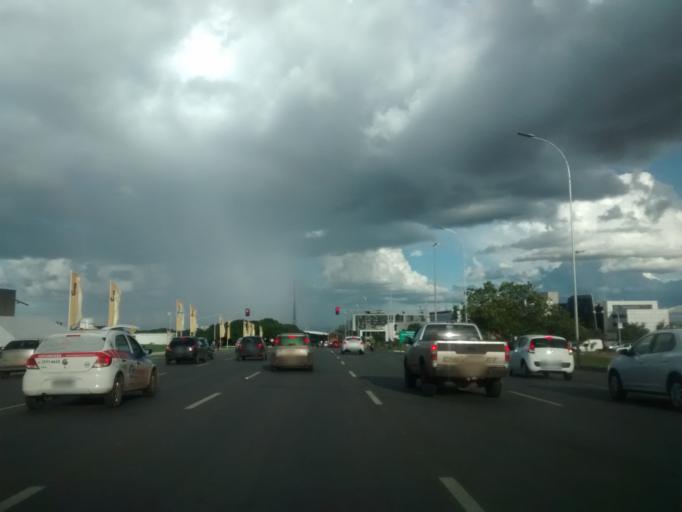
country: BR
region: Federal District
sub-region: Brasilia
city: Brasilia
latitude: -15.7848
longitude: -47.9147
